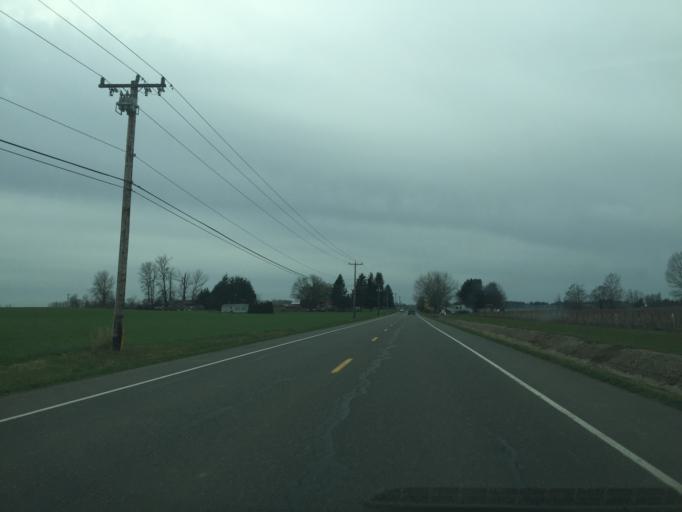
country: US
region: Washington
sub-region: Whatcom County
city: Everson
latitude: 48.9420
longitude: -122.3875
